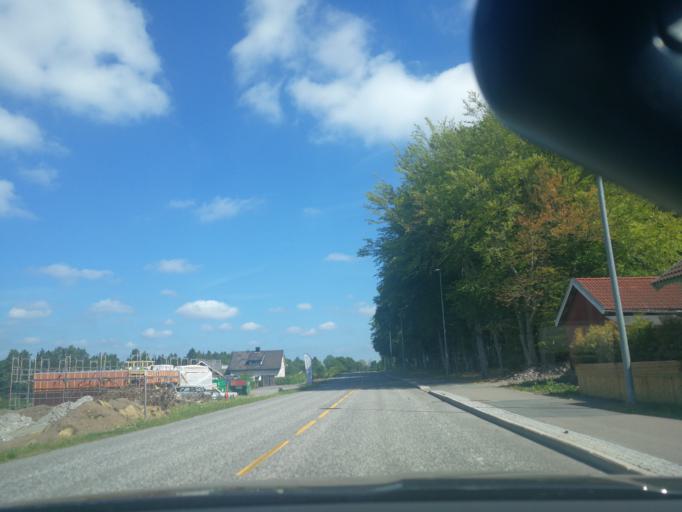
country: NO
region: Vestfold
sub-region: Stokke
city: Stokke
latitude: 59.1997
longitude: 10.2338
